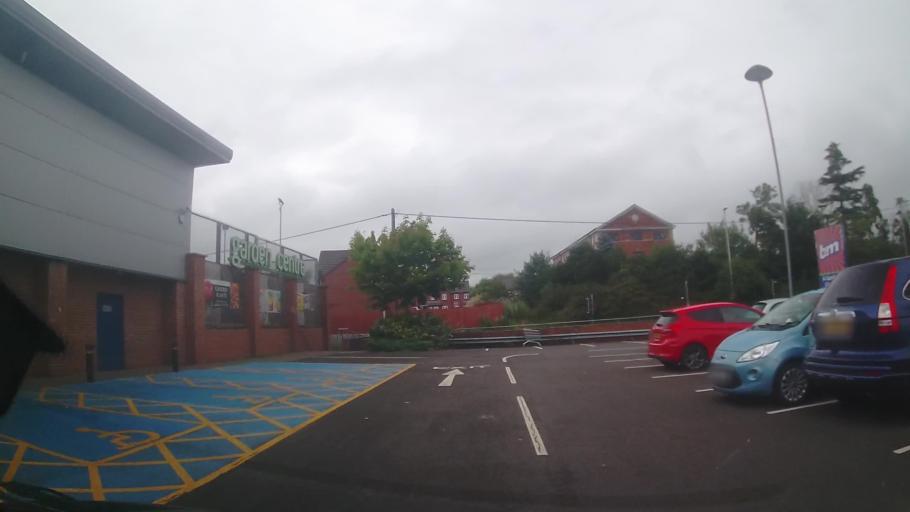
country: GB
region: England
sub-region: Shropshire
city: Whitchurch
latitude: 52.9666
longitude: -2.6698
